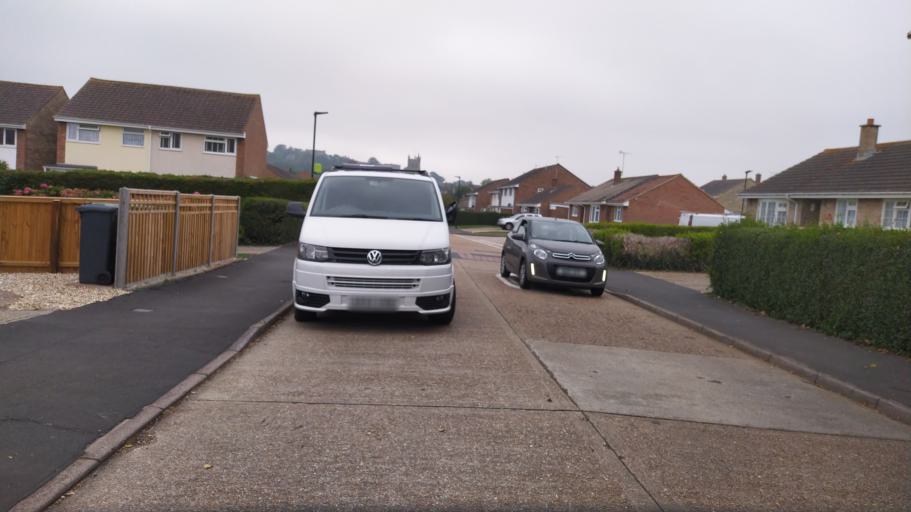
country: GB
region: England
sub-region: Isle of Wight
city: Newport
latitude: 50.6958
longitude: -1.3136
